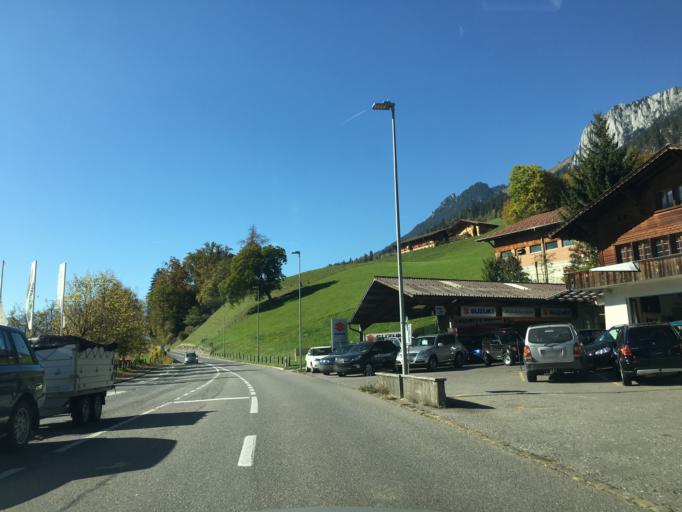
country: CH
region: Bern
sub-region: Frutigen-Niedersimmental District
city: Erlenbach im Simmental
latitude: 46.6599
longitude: 7.5455
